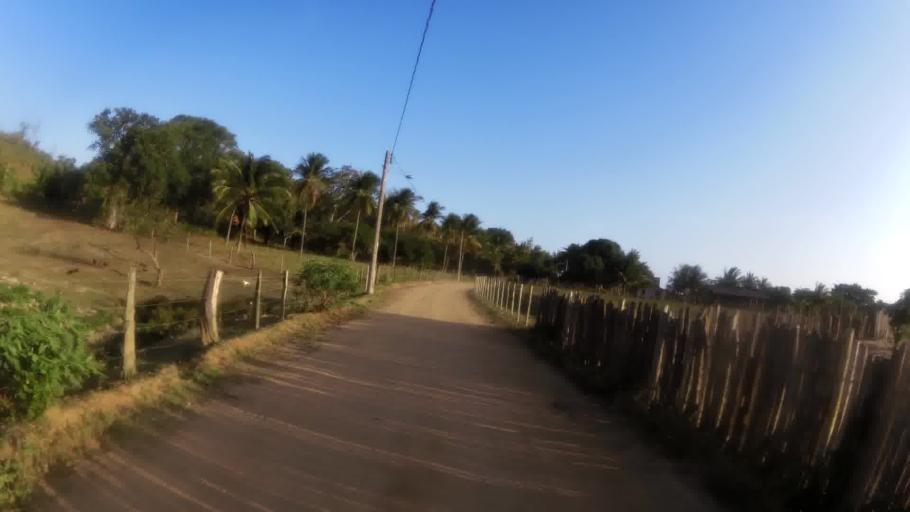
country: BR
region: Espirito Santo
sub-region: Piuma
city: Piuma
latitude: -20.8837
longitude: -40.7825
